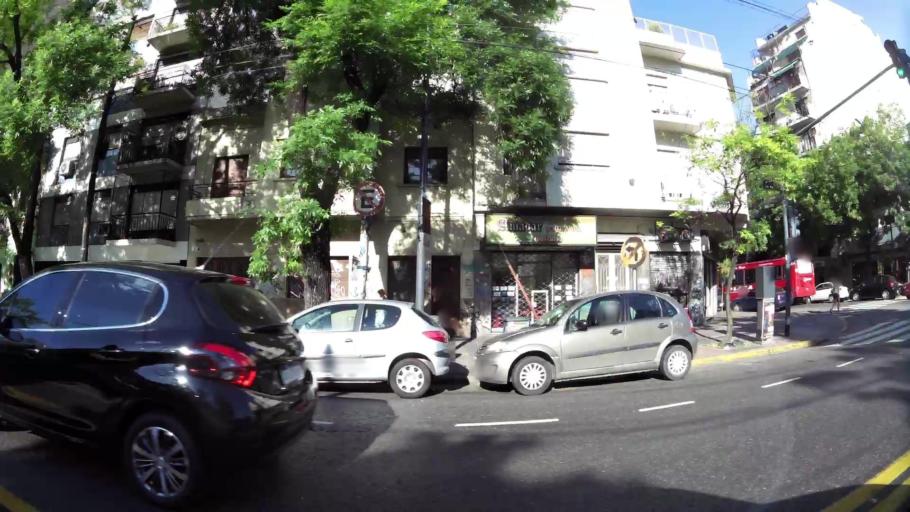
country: AR
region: Buenos Aires F.D.
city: Colegiales
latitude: -34.6141
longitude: -58.4379
